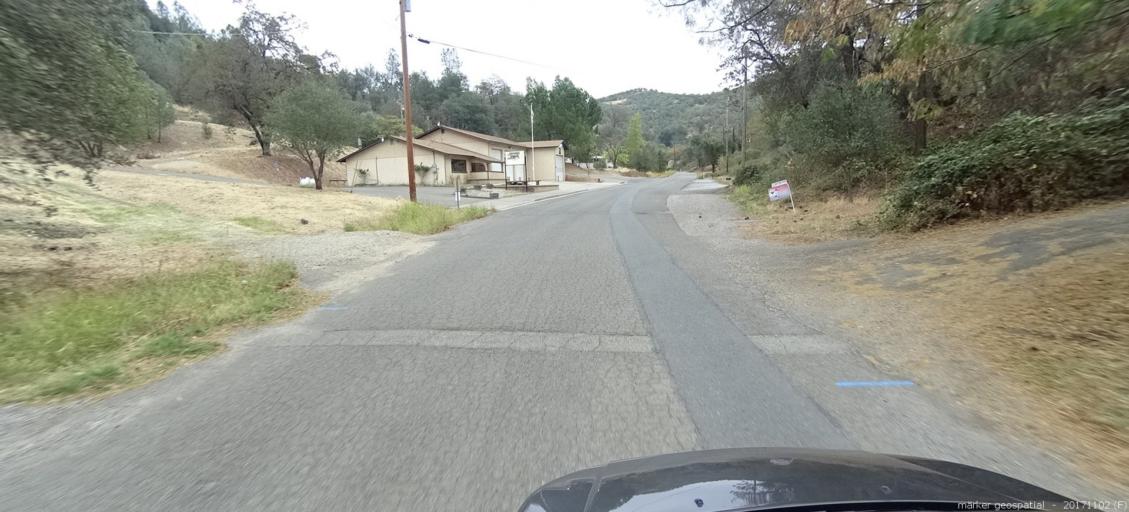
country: US
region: California
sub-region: Shasta County
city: Bella Vista
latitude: 40.7143
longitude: -122.2396
